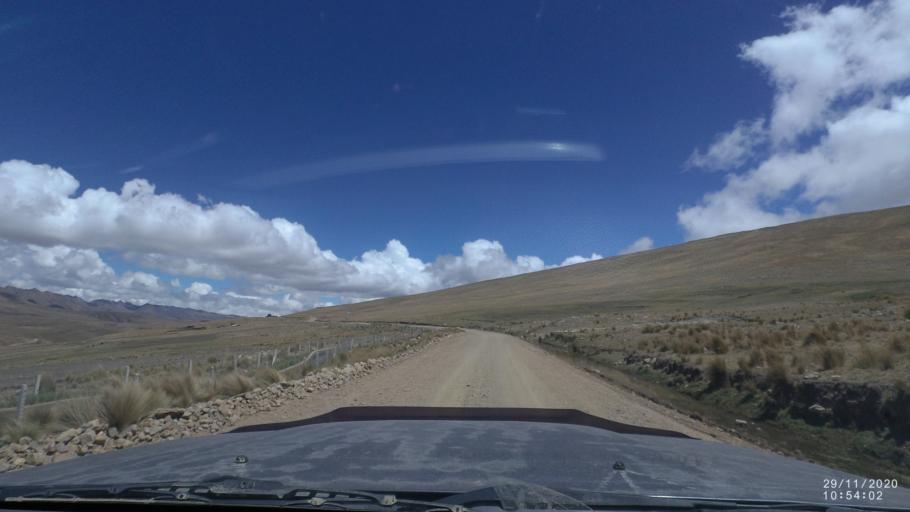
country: BO
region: Cochabamba
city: Cochabamba
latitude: -17.2308
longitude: -66.2176
